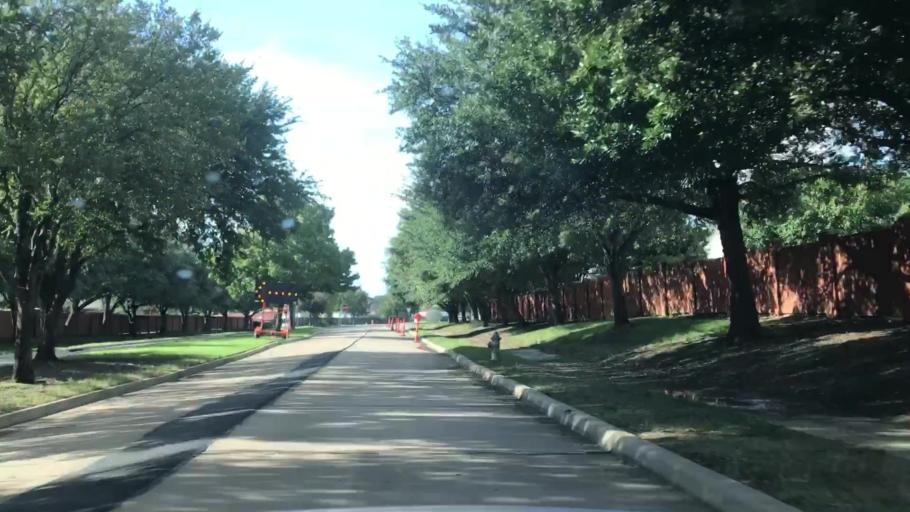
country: US
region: Texas
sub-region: Dallas County
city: Coppell
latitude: 32.9348
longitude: -96.9619
